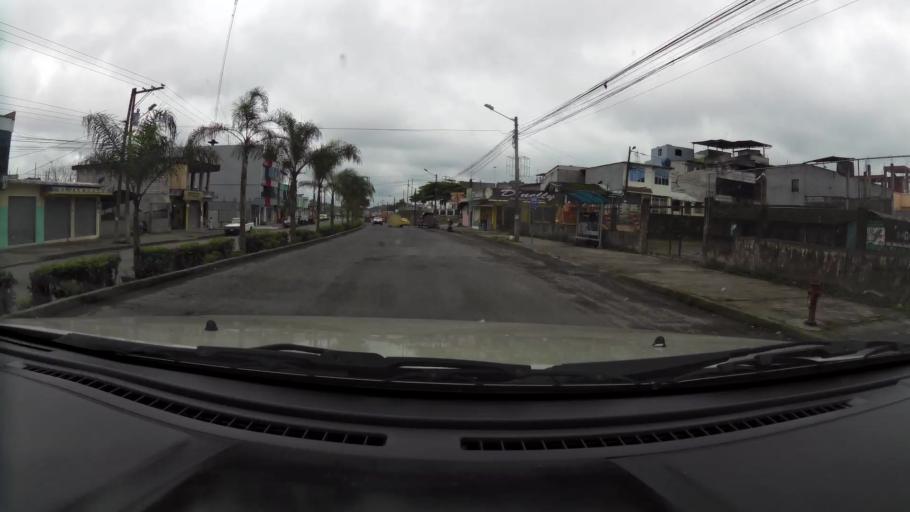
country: EC
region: Santo Domingo de los Tsachilas
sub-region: Canton Santo Domingo de los Colorados
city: Santo Domingo de los Colorados
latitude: -0.2362
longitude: -79.1672
